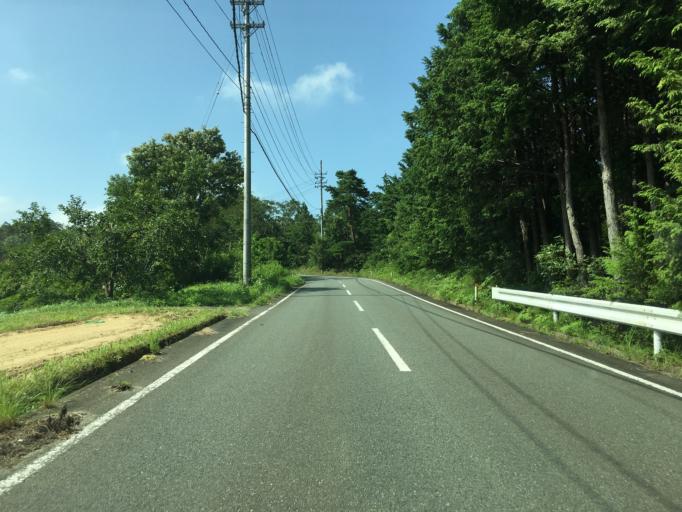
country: JP
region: Miyagi
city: Marumori
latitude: 37.8946
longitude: 140.8902
